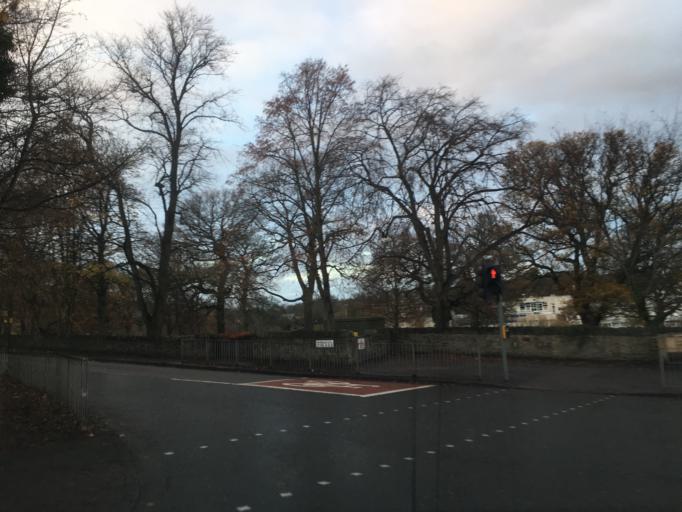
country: GB
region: Scotland
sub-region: Edinburgh
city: Colinton
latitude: 55.9502
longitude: -3.2508
